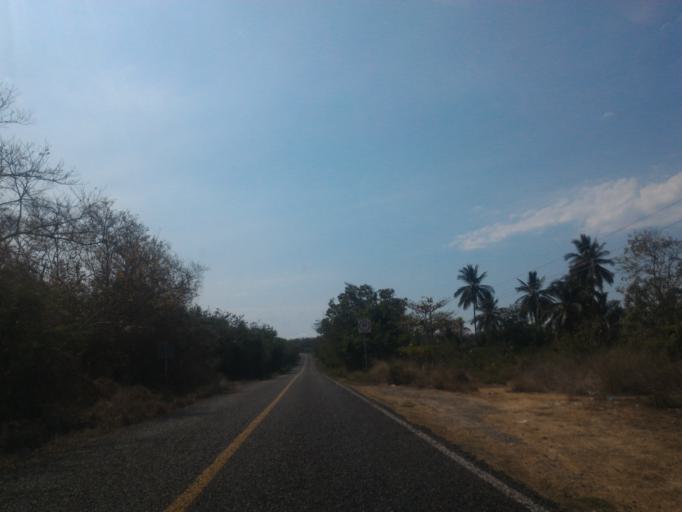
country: MX
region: Michoacan
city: Coahuayana Viejo
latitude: 18.3921
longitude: -103.5259
